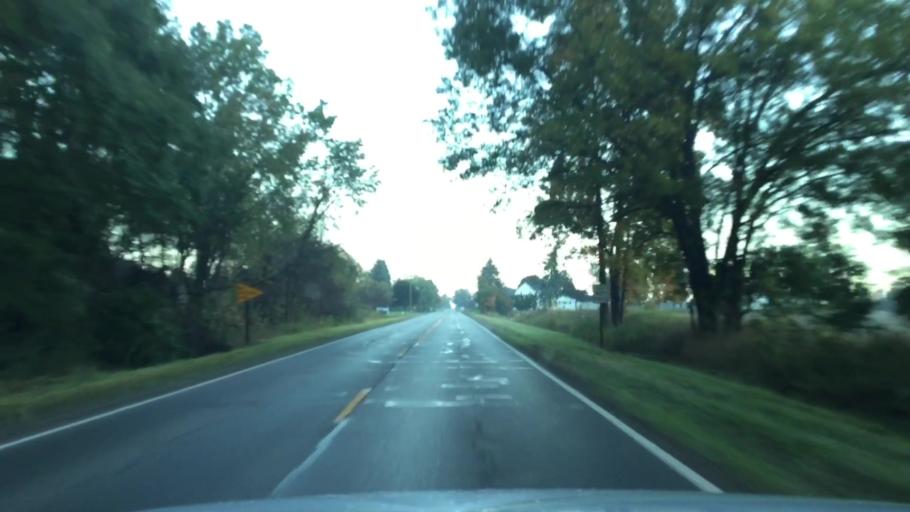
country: US
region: Michigan
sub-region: Livingston County
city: Howell
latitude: 42.6592
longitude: -83.9356
